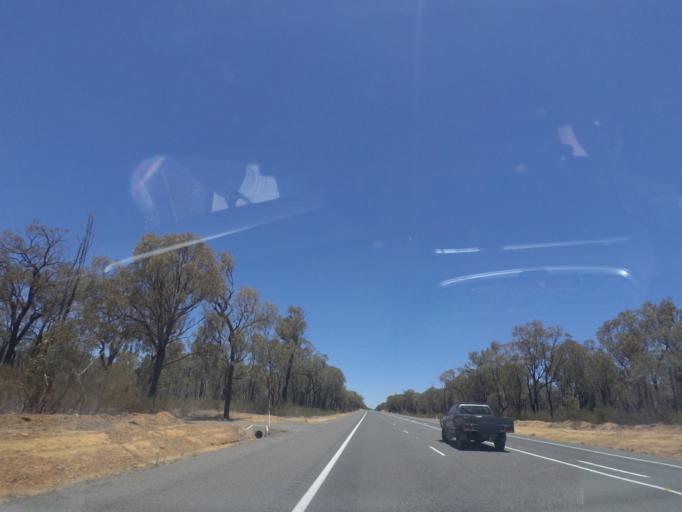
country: AU
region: New South Wales
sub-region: Warrumbungle Shire
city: Coonabarabran
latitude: -30.8970
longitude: 149.4405
